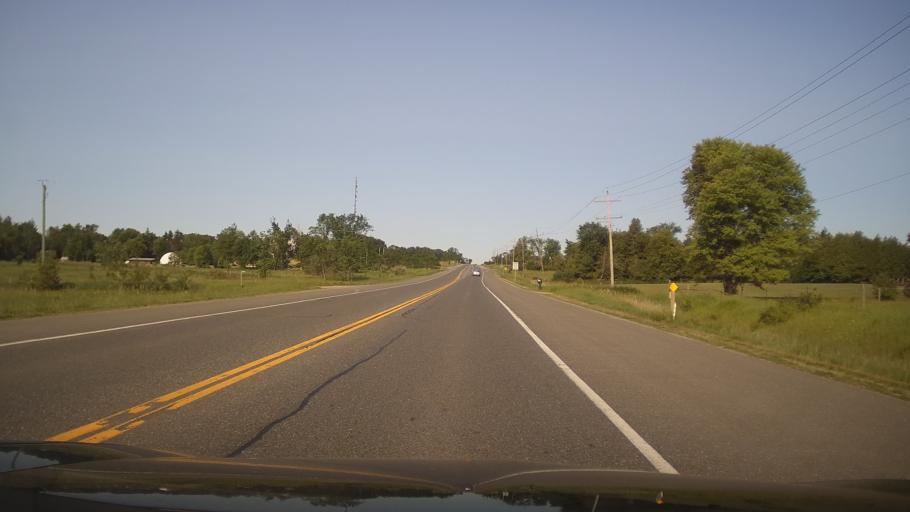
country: CA
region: Ontario
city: Peterborough
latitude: 44.3583
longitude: -78.0341
